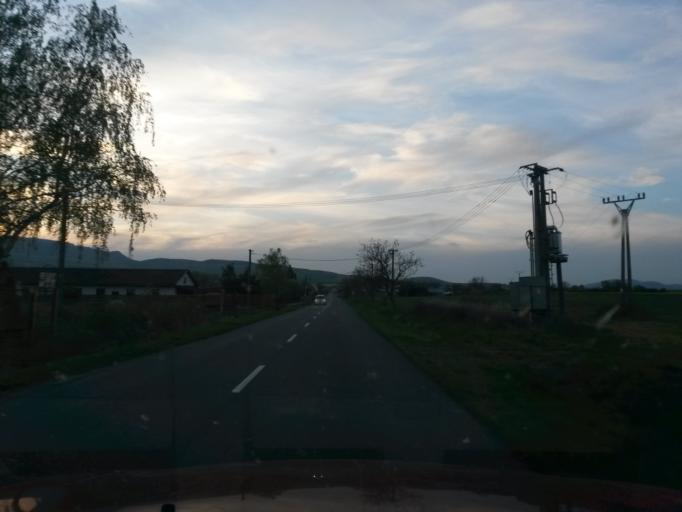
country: SK
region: Kosicky
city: Trebisov
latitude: 48.5455
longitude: 21.5629
